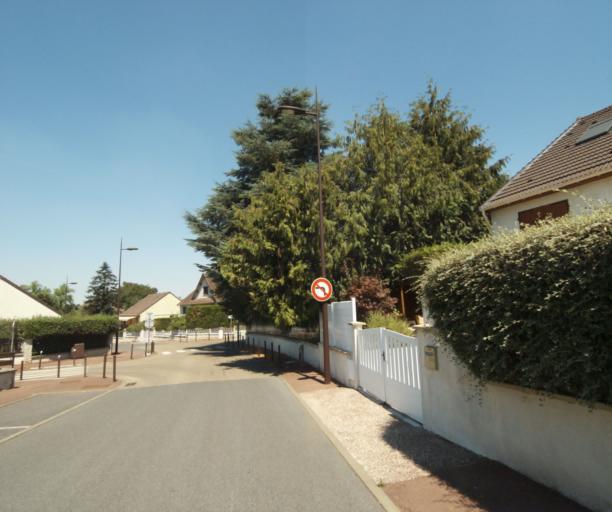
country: FR
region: Ile-de-France
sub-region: Departement de Seine-et-Marne
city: Lagny-sur-Marne
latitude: 48.8754
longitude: 2.7292
